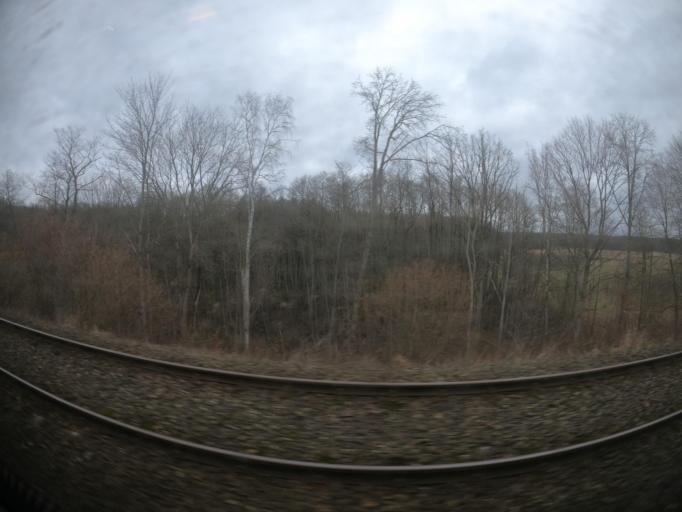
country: PL
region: West Pomeranian Voivodeship
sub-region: Powiat drawski
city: Drawsko Pomorskie
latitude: 53.5211
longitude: 15.6933
